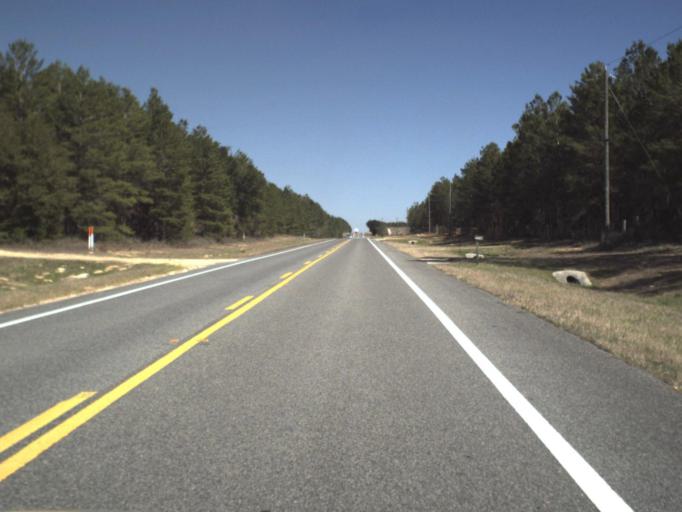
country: US
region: Florida
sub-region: Bay County
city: Lynn Haven
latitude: 30.4264
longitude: -85.6233
